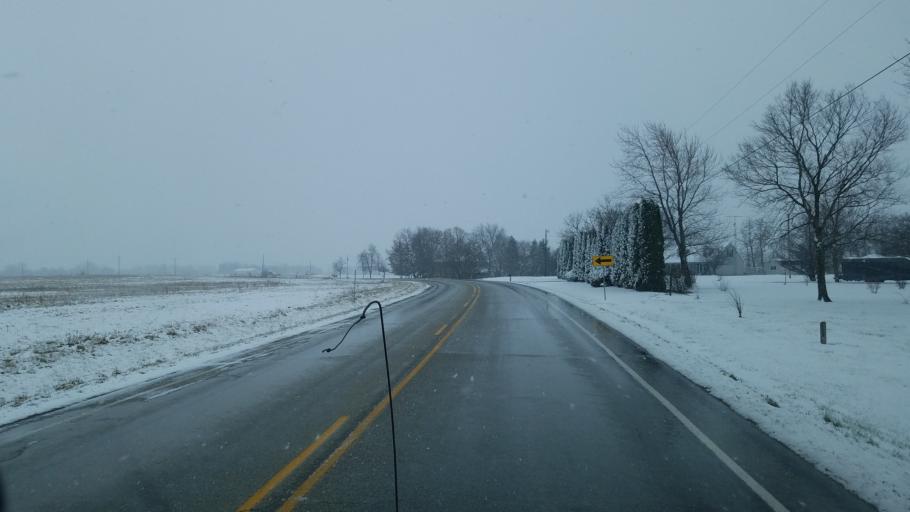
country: US
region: Indiana
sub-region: Randolph County
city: Lynn
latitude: 39.9415
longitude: -84.9840
